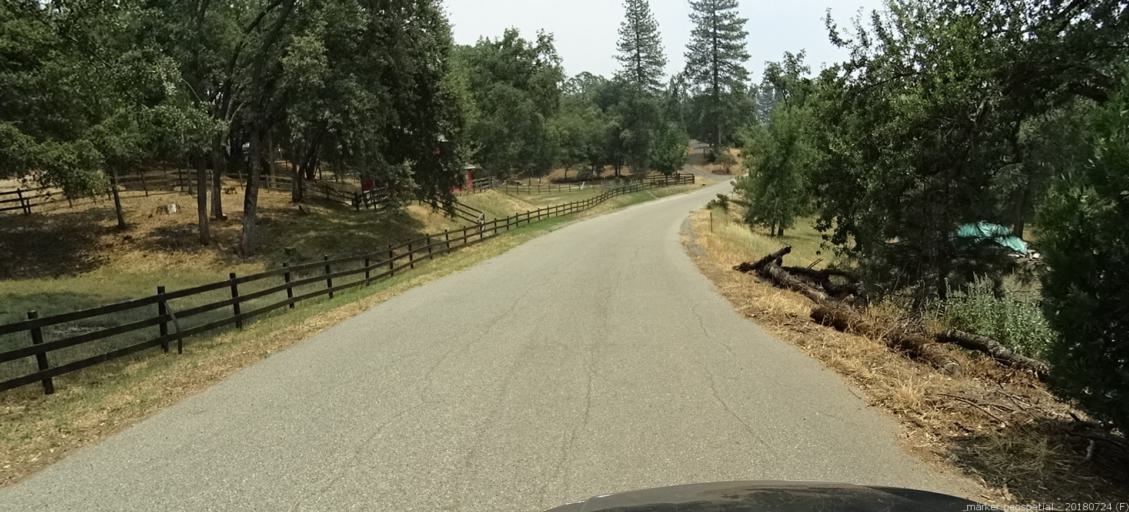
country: US
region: California
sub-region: Madera County
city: Oakhurst
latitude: 37.2762
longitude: -119.5824
